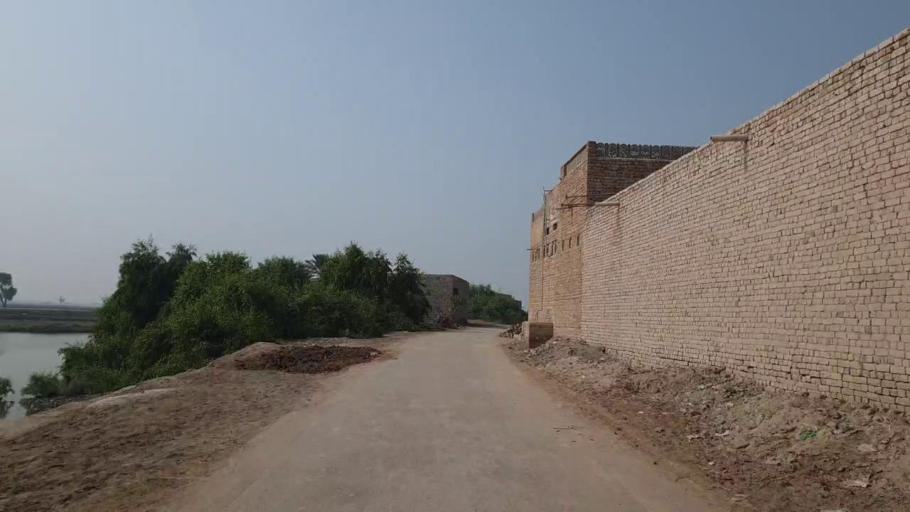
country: PK
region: Sindh
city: Bhan
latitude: 26.4435
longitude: 67.7235
